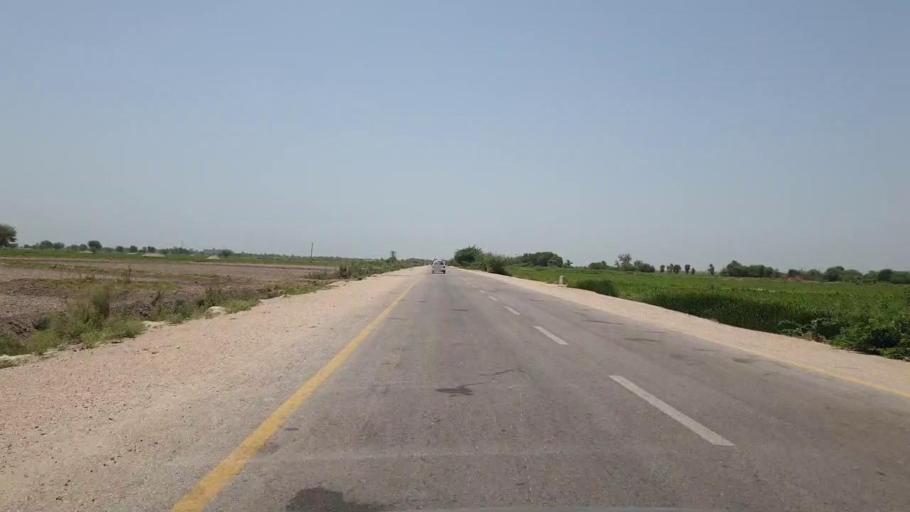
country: PK
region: Sindh
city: Sakrand
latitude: 26.1323
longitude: 68.3756
